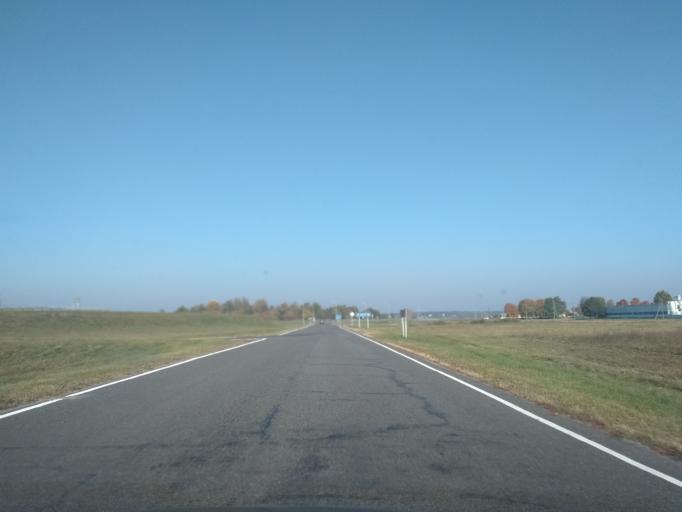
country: BY
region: Brest
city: Ivatsevichy
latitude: 52.6974
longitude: 25.3646
